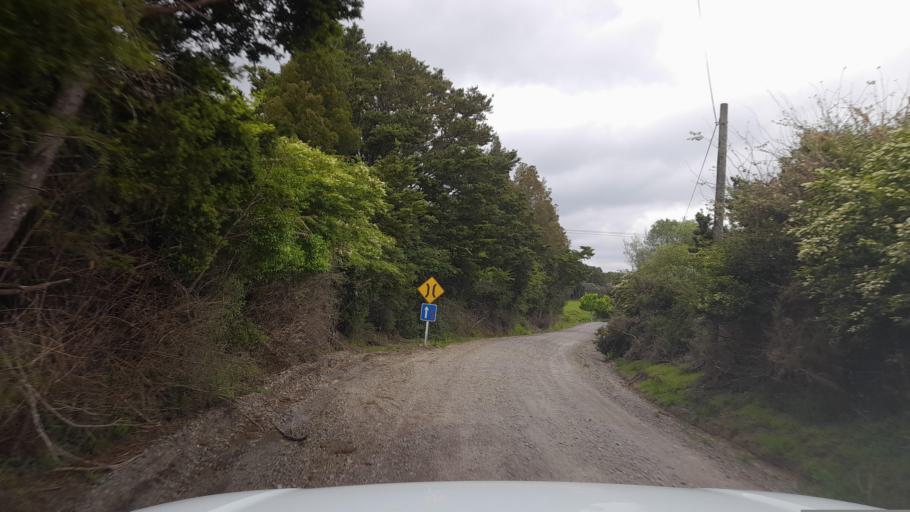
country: NZ
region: Northland
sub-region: Far North District
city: Waimate North
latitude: -35.3982
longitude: 173.7847
